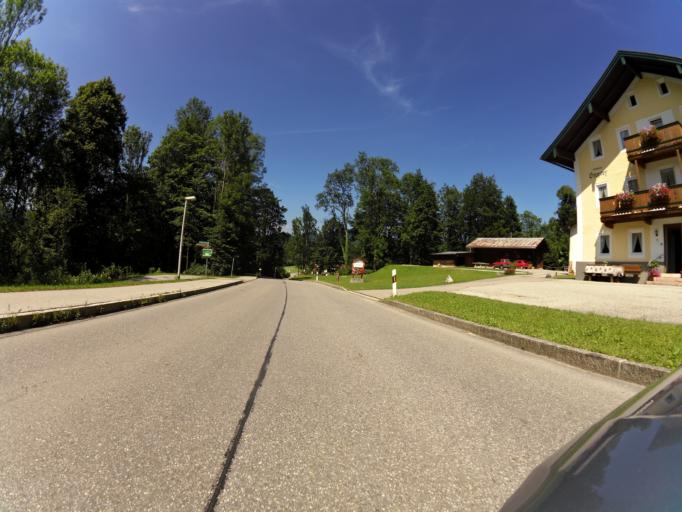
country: DE
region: Bavaria
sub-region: Upper Bavaria
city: Schoenau am Koenigssee
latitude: 47.6158
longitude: 12.9823
